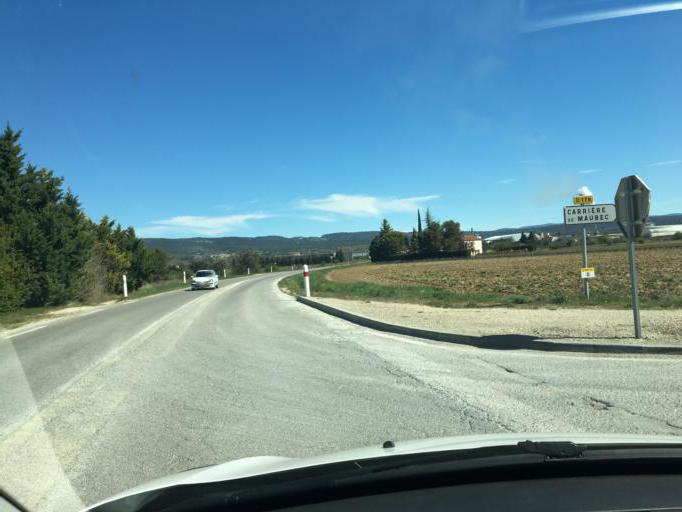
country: FR
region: Provence-Alpes-Cote d'Azur
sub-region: Departement du Vaucluse
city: Maubec
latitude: 43.8609
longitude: 5.1342
